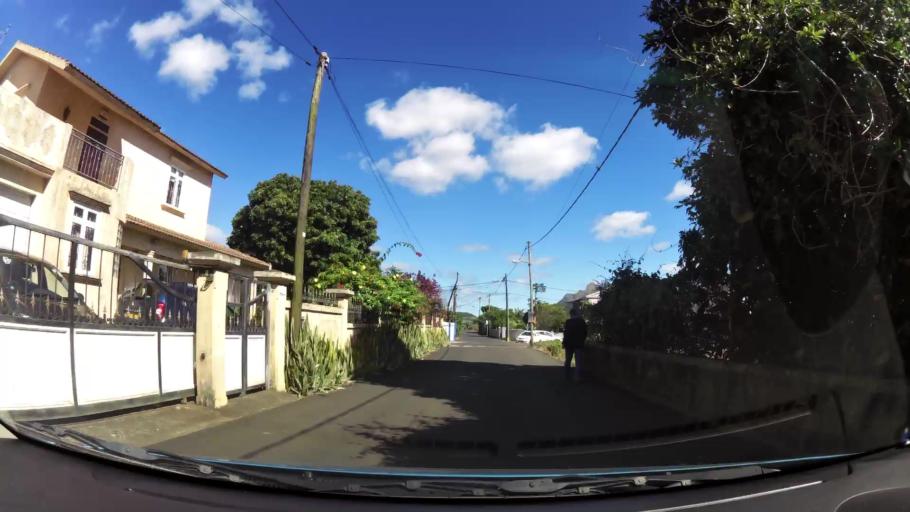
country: MU
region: Plaines Wilhems
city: Vacoas
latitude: -20.2931
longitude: 57.4735
